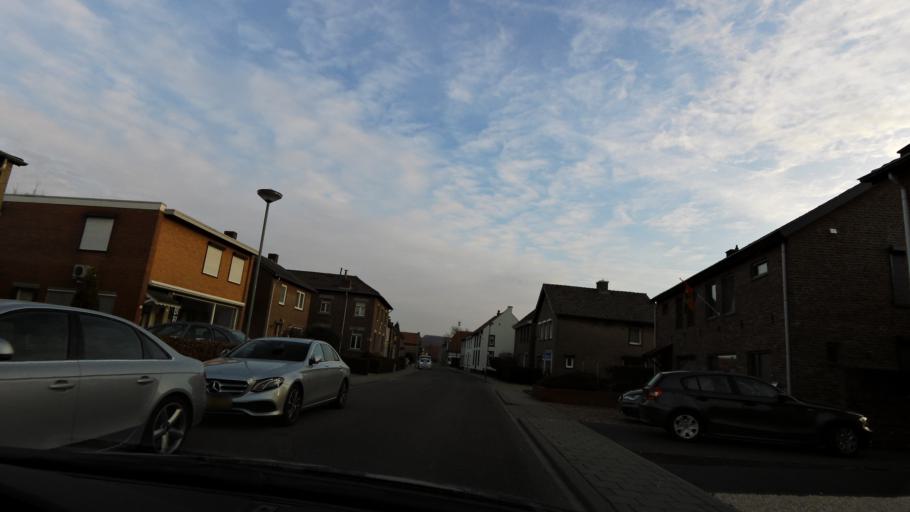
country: NL
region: Limburg
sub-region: Gemeente Schinnen
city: Puth
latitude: 50.9393
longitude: 5.8415
